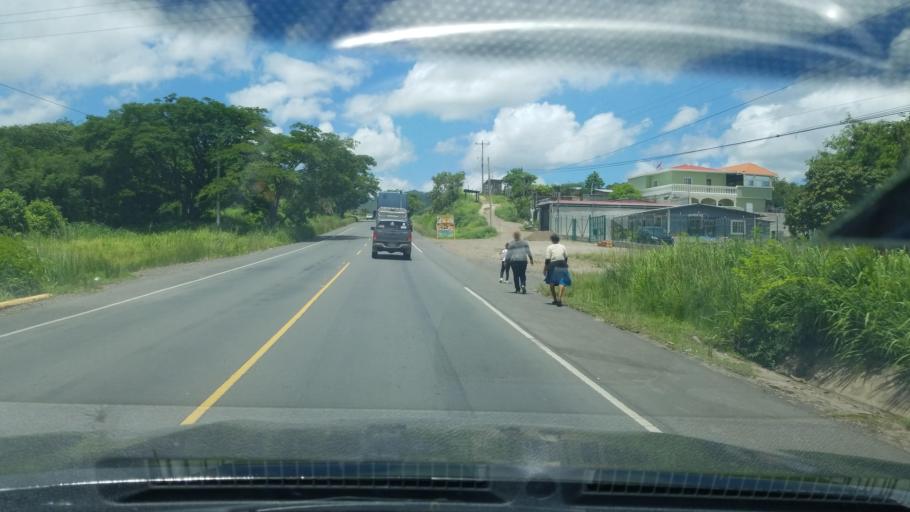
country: HN
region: Francisco Morazan
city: Cofradia
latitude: 14.2648
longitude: -87.2448
